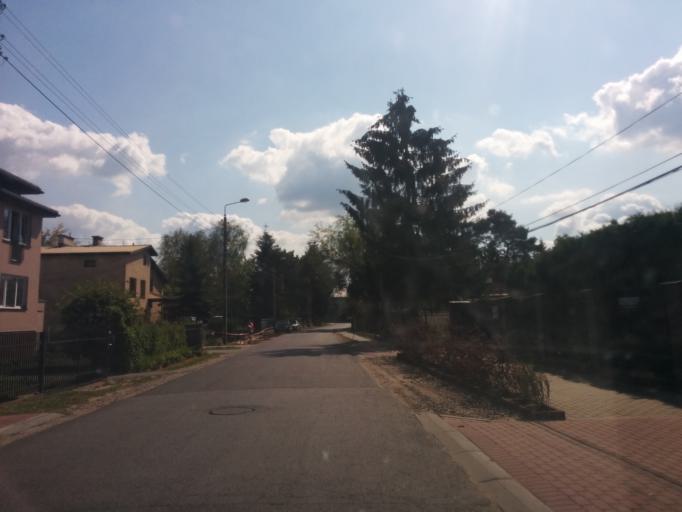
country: PL
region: Masovian Voivodeship
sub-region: Warszawa
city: Bialoleka
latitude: 52.3417
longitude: 20.9850
